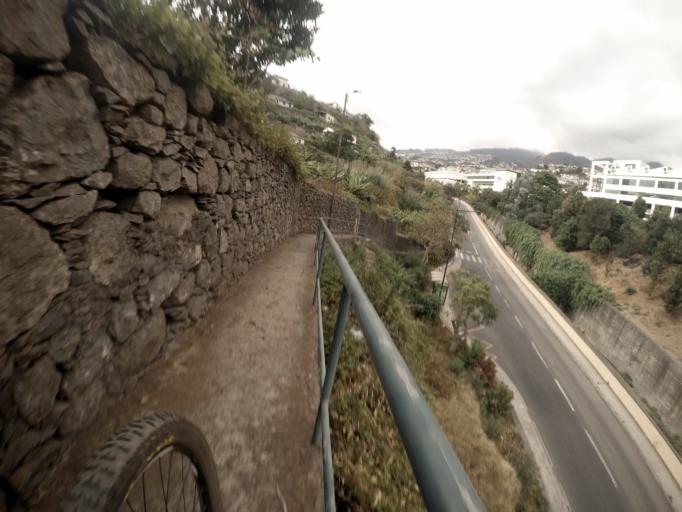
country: PT
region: Madeira
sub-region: Funchal
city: Nossa Senhora do Monte
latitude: 32.6574
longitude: -16.9246
